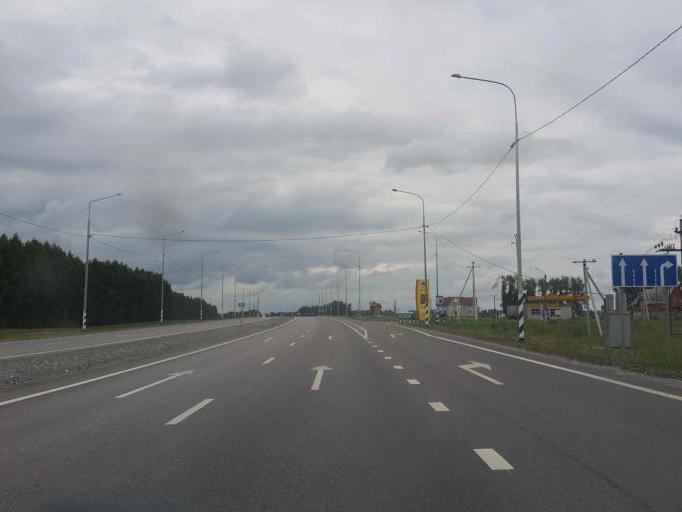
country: RU
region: Tambov
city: Zavoronezhskoye
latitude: 52.8639
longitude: 40.7635
